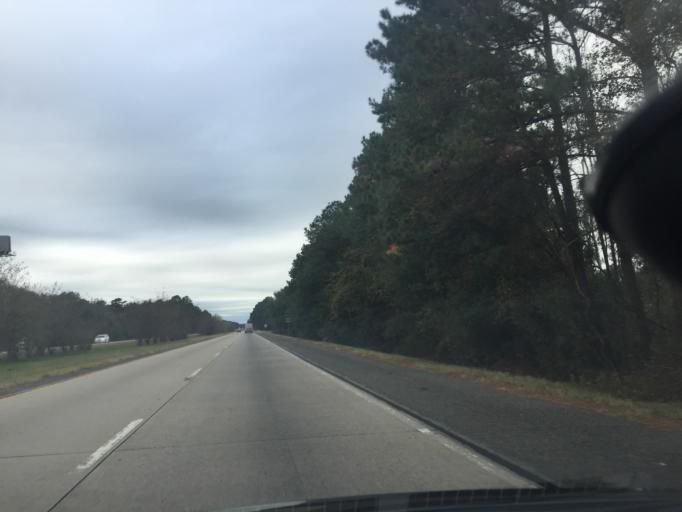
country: US
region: Georgia
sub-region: Chatham County
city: Bloomingdale
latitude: 32.1300
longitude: -81.3950
